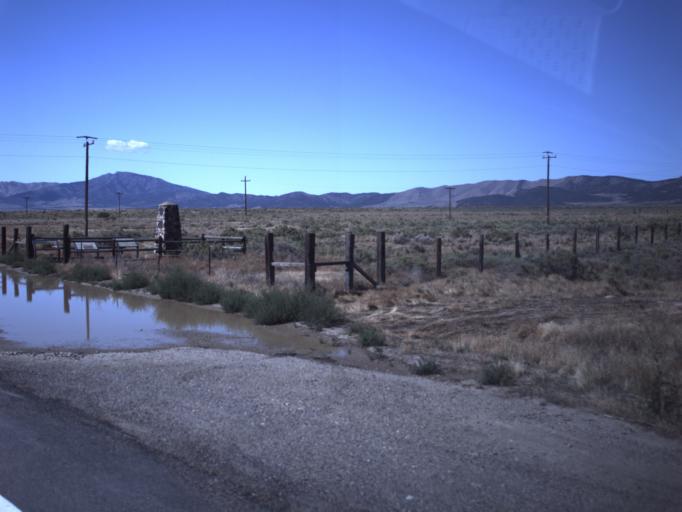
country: US
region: Utah
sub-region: Tooele County
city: Tooele
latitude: 40.1745
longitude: -112.4271
